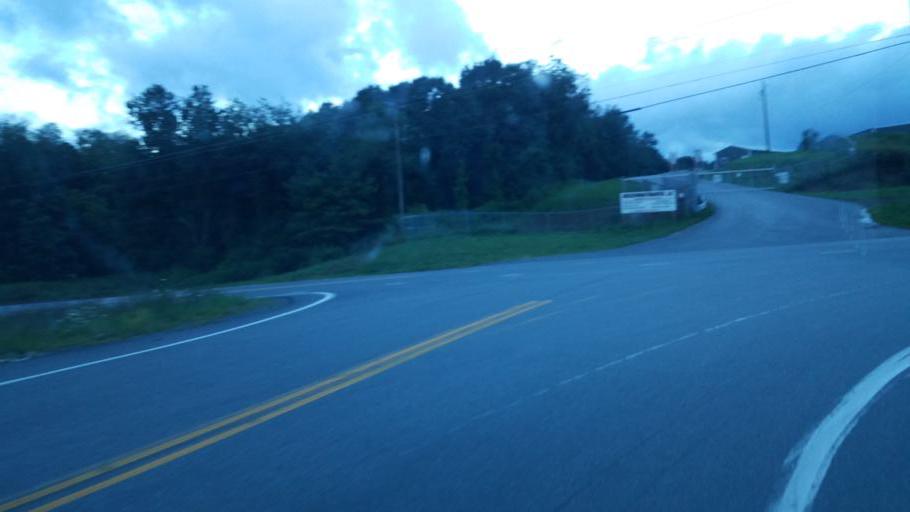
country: US
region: Pennsylvania
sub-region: Bedford County
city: Earlston
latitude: 39.9789
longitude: -78.2454
